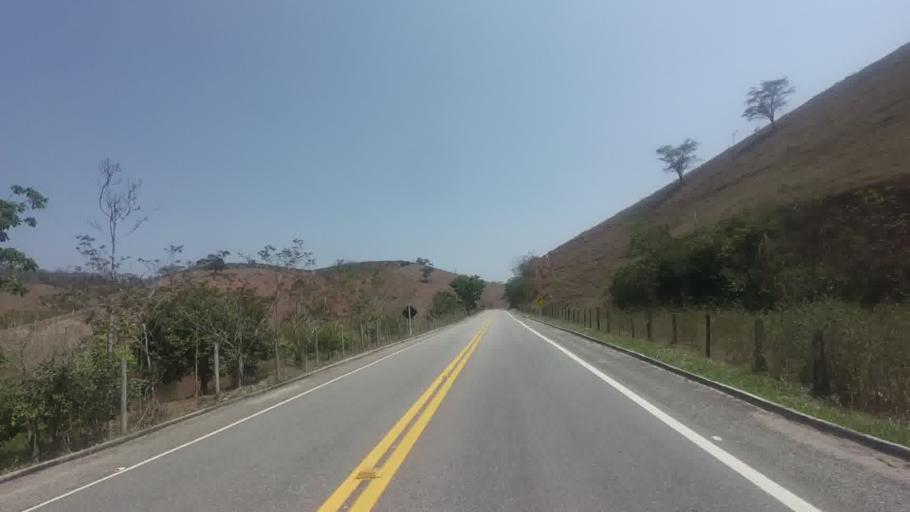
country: BR
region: Espirito Santo
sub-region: Jeronimo Monteiro
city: Jeronimo Monteiro
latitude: -20.8853
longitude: -41.2724
